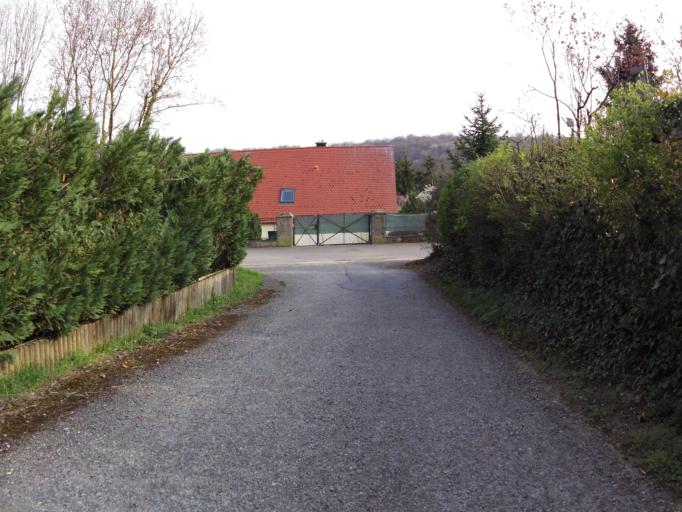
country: DE
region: Bavaria
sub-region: Regierungsbezirk Unterfranken
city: Rottendorf
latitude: 49.7868
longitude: 10.0187
